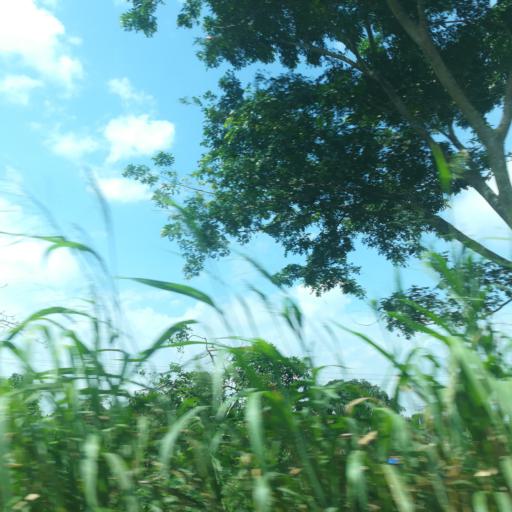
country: NG
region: Lagos
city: Ikorodu
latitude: 6.6617
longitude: 3.6791
